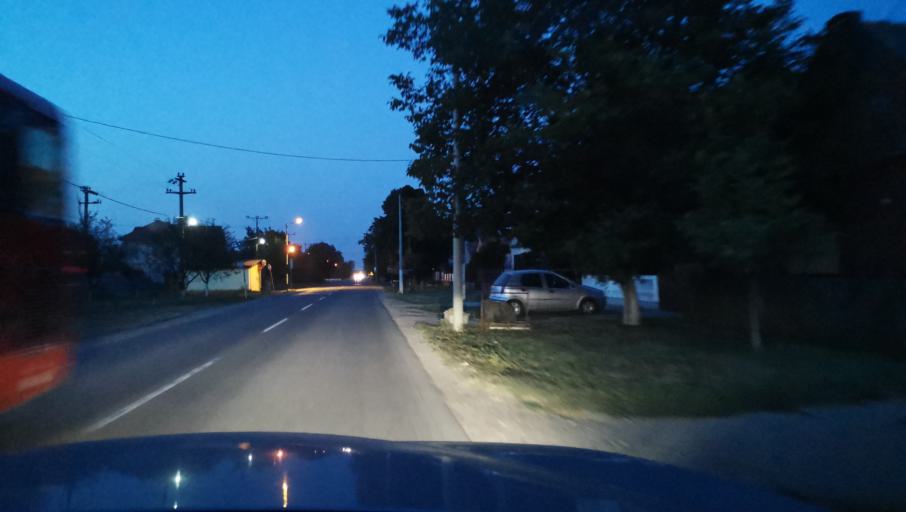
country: RS
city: Boljevci
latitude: 44.7270
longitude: 20.2407
